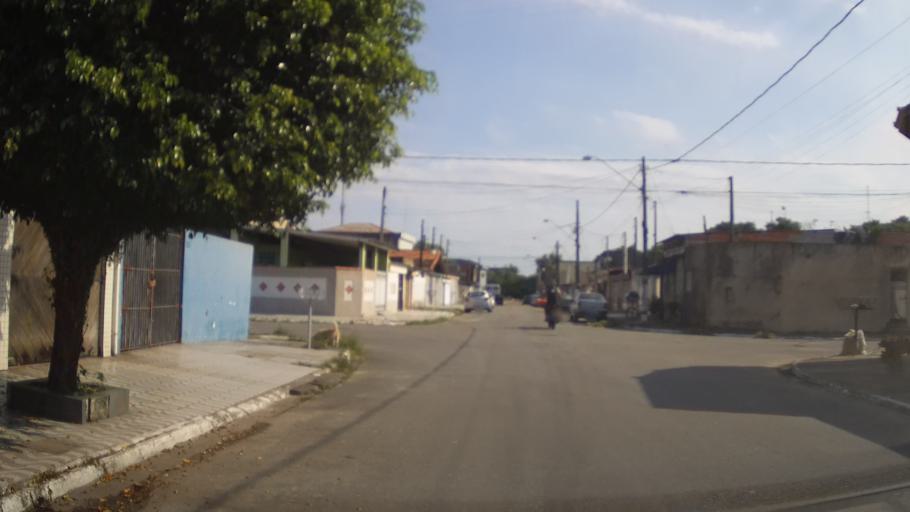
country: BR
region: Sao Paulo
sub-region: Praia Grande
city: Praia Grande
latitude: -24.0011
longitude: -46.4328
